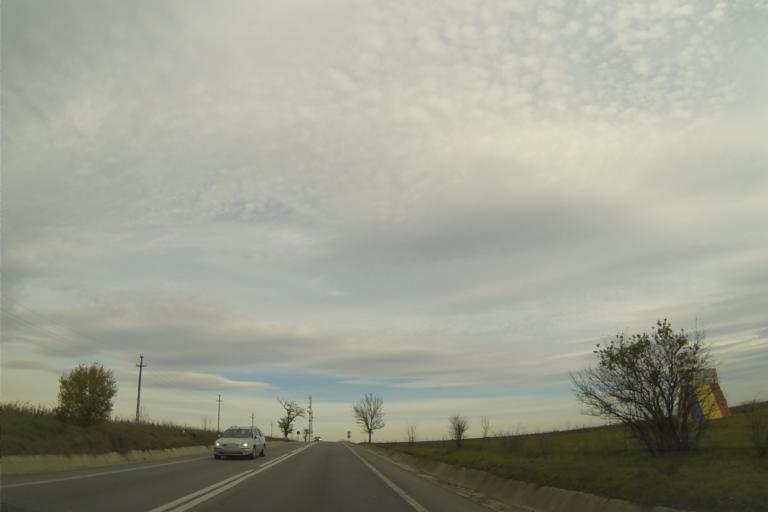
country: RO
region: Olt
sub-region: Comuna Valea Mare
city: Valea Mare
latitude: 44.4726
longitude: 24.4243
